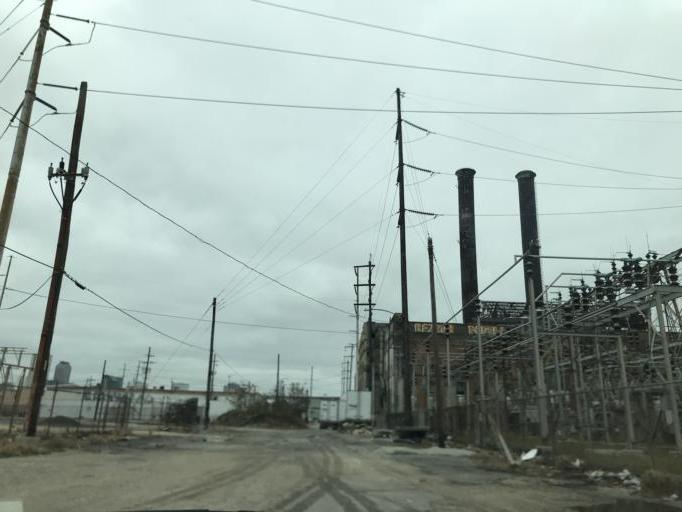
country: US
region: Louisiana
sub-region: Jefferson Parish
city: Gretna
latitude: 29.9287
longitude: -90.0653
